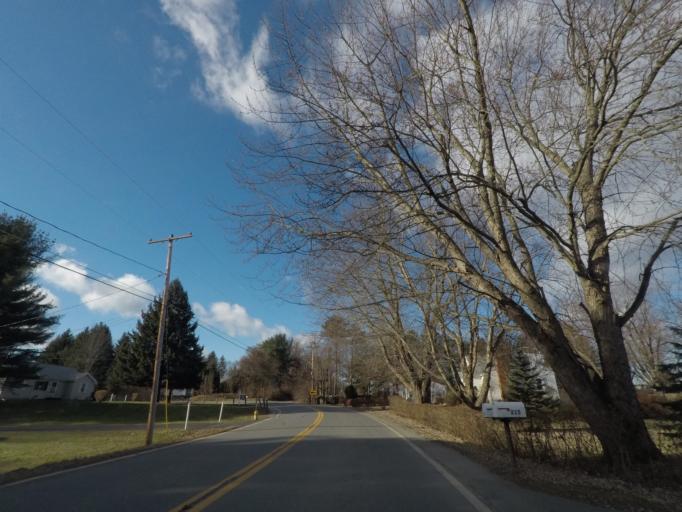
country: US
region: New York
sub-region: Saratoga County
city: Waterford
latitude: 42.8300
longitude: -73.7084
